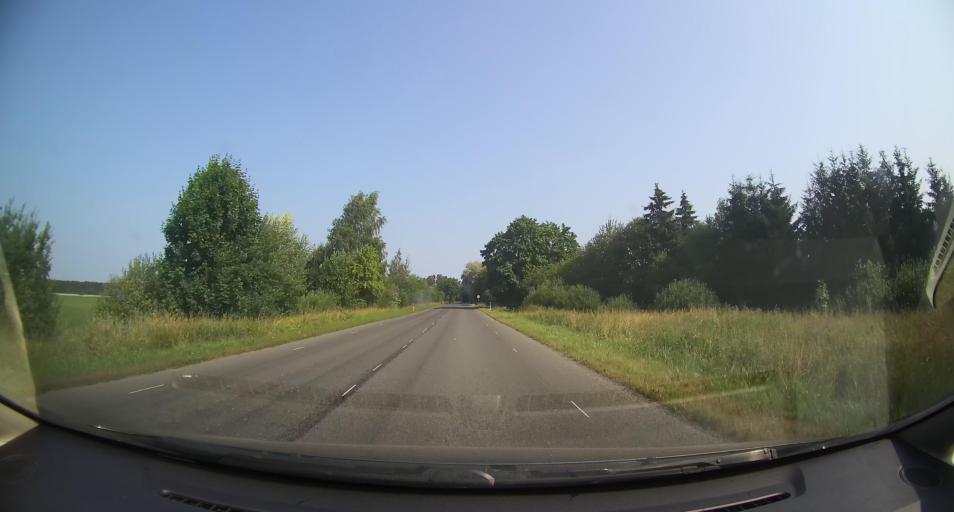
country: EE
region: Paernumaa
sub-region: Audru vald
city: Audru
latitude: 58.4885
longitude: 24.3356
